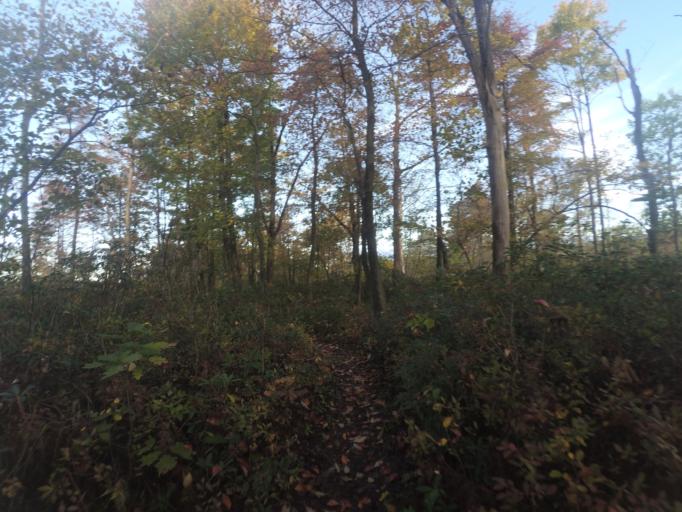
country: US
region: Pennsylvania
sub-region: Centre County
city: Stormstown
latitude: 40.8901
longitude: -77.9966
